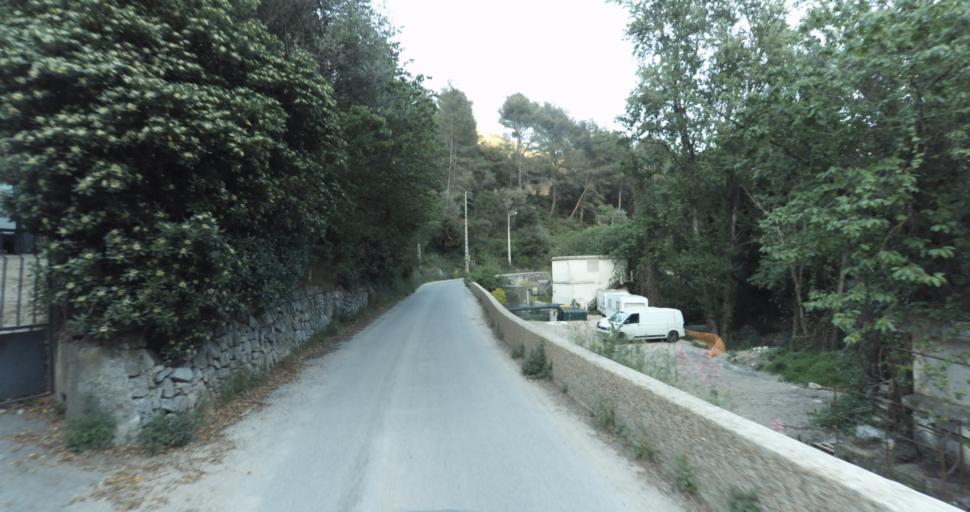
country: FR
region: Provence-Alpes-Cote d'Azur
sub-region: Departement du Var
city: Le Revest-les-Eaux
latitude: 43.1736
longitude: 5.9313
